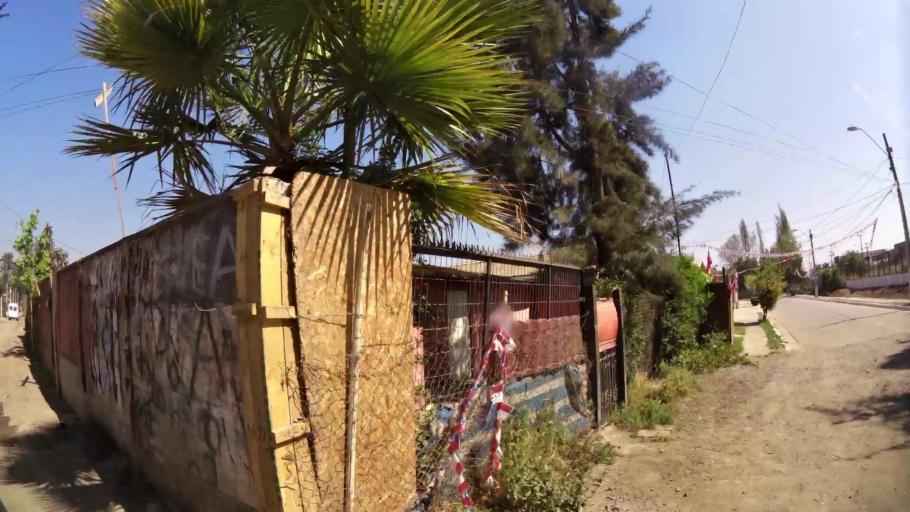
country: CL
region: Santiago Metropolitan
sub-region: Provincia de Talagante
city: Penaflor
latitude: -33.5773
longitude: -70.8098
